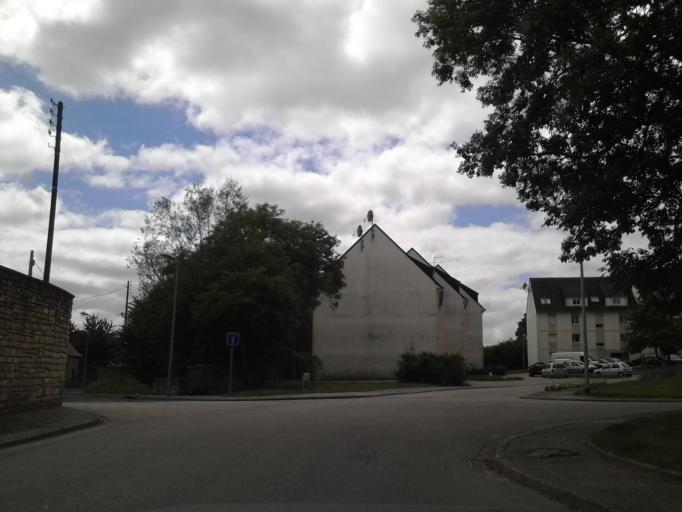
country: FR
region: Lower Normandy
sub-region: Departement de la Manche
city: Valognes
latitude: 49.5144
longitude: -1.4753
